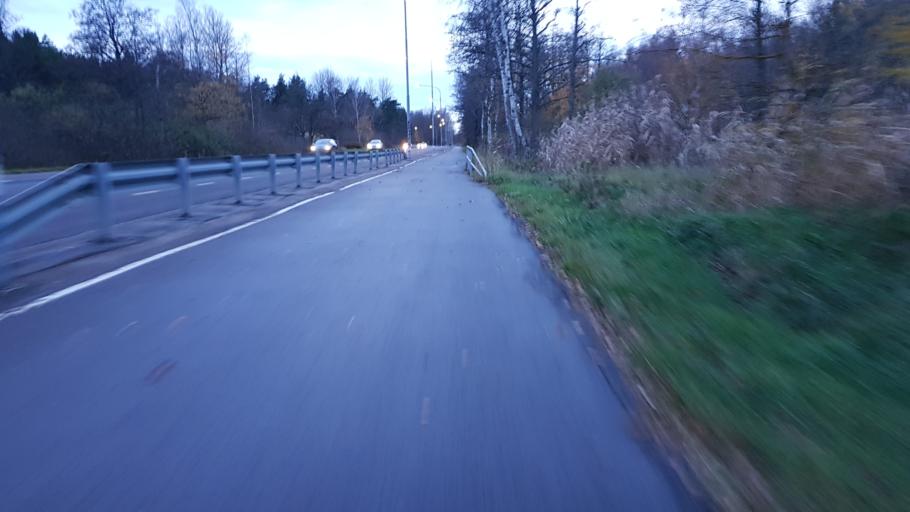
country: SE
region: OEstergoetland
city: Lindo
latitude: 58.5989
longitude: 16.2398
